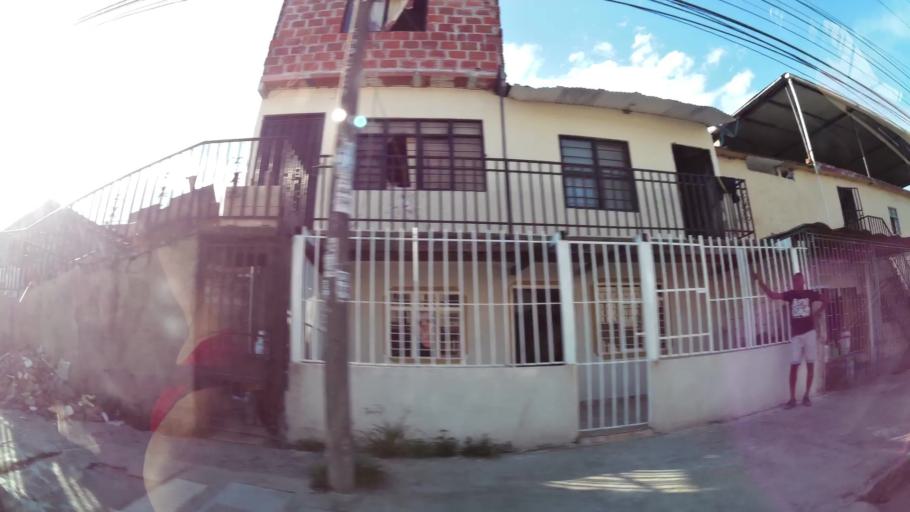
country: CO
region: Valle del Cauca
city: Cali
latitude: 3.4101
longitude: -76.5090
